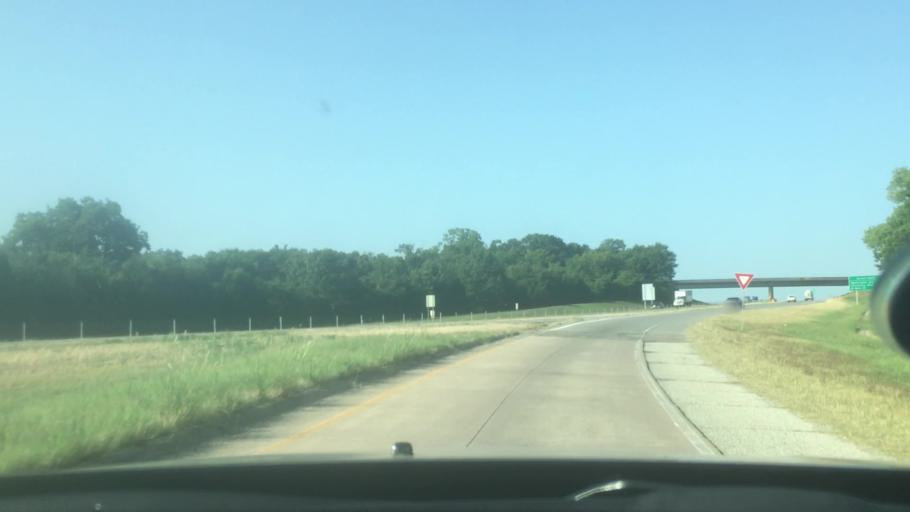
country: US
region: Oklahoma
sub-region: Bryan County
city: Durant
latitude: 34.0363
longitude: -96.3777
